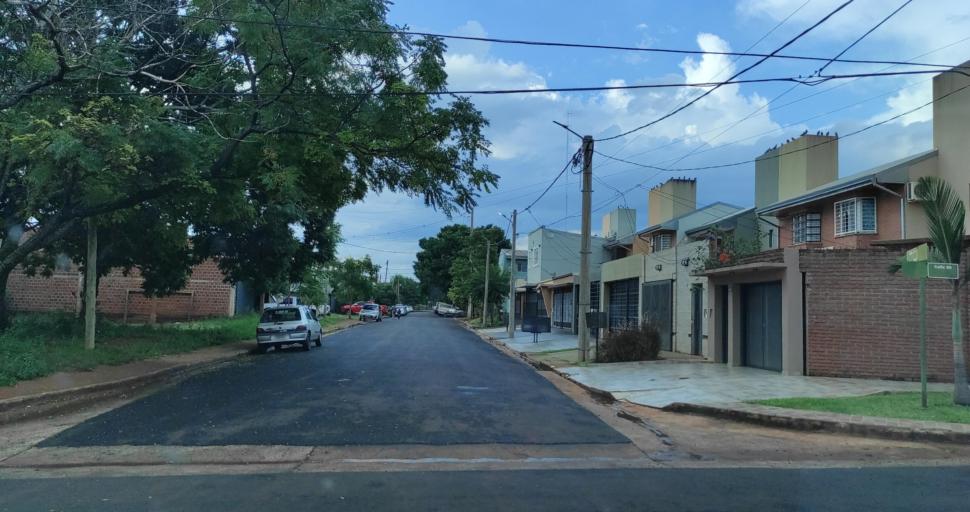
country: AR
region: Misiones
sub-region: Departamento de Capital
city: Posadas
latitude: -27.3734
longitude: -55.9306
